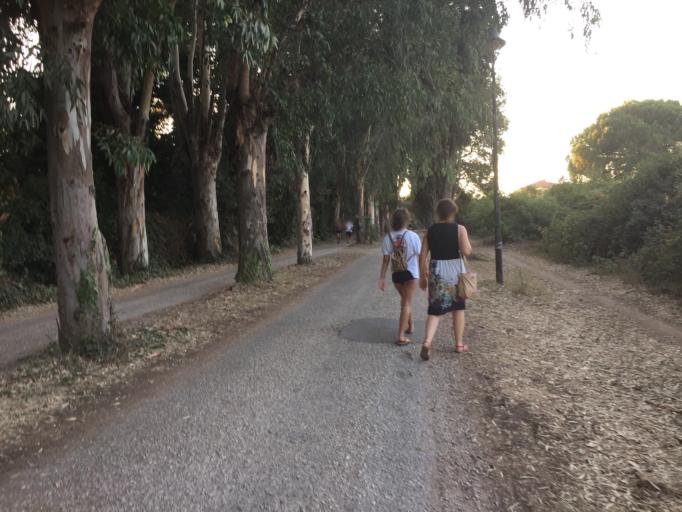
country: IT
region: Latium
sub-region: Citta metropolitana di Roma Capitale
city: Marina San Nicola
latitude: 41.9381
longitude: 12.1045
